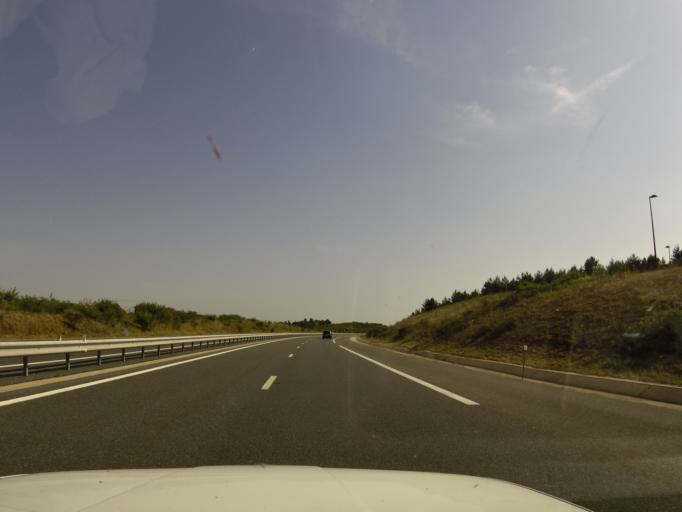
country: FR
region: Midi-Pyrenees
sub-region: Departement de l'Aveyron
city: Millau
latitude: 44.1704
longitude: 3.0310
